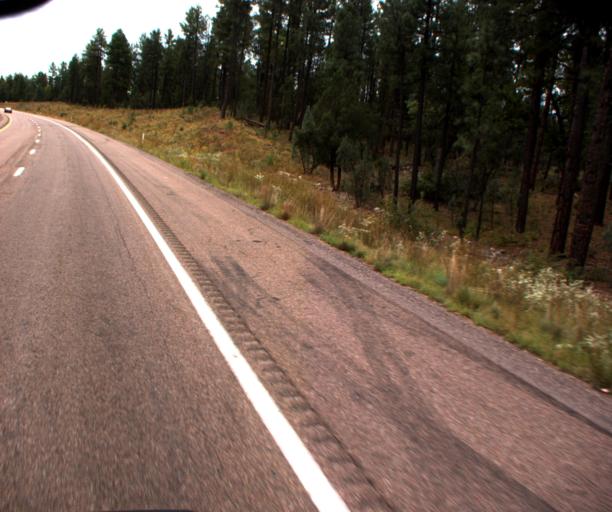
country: US
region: Arizona
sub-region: Gila County
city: Star Valley
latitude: 34.2989
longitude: -110.9882
